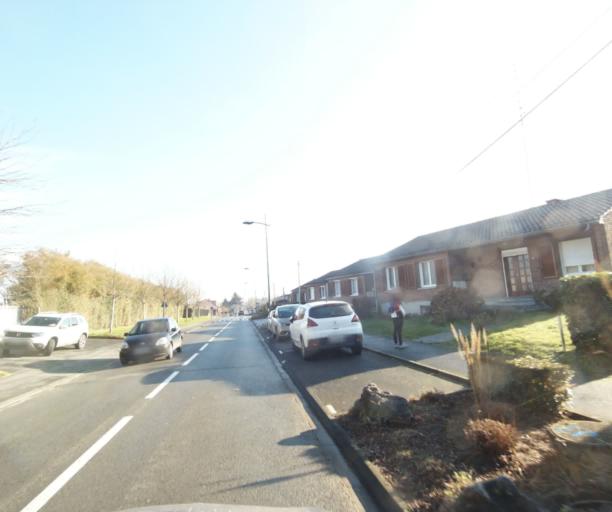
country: FR
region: Nord-Pas-de-Calais
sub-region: Departement du Nord
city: Aulnoy-lez-Valenciennes
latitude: 50.3335
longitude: 3.5249
